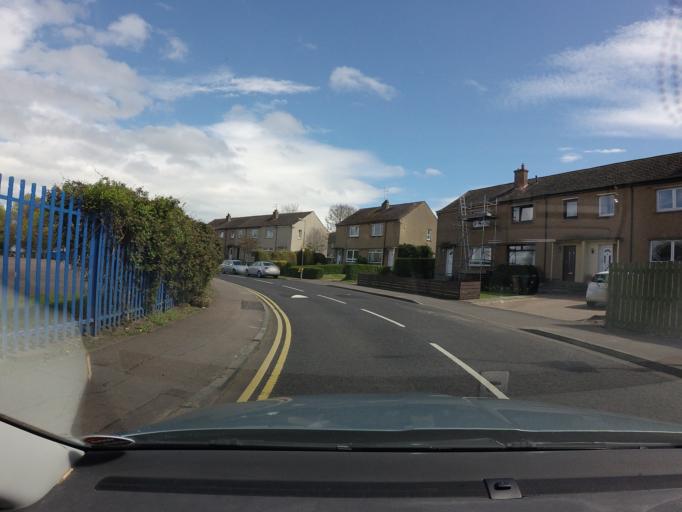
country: GB
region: Scotland
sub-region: Edinburgh
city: Queensferry
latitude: 55.9869
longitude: -3.3939
